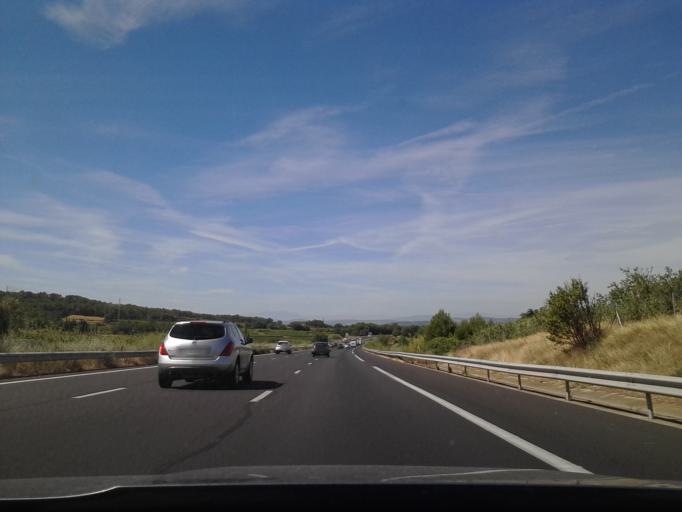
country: FR
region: Languedoc-Roussillon
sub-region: Departement de l'Aude
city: Vinassan
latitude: 43.1974
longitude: 3.0761
